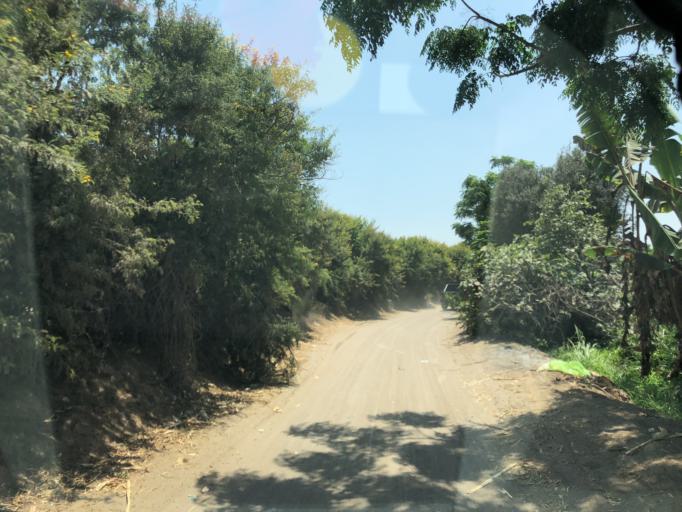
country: PE
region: Lima
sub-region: Provincia de Canete
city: San Vicente de Canete
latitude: -13.0106
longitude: -76.4653
